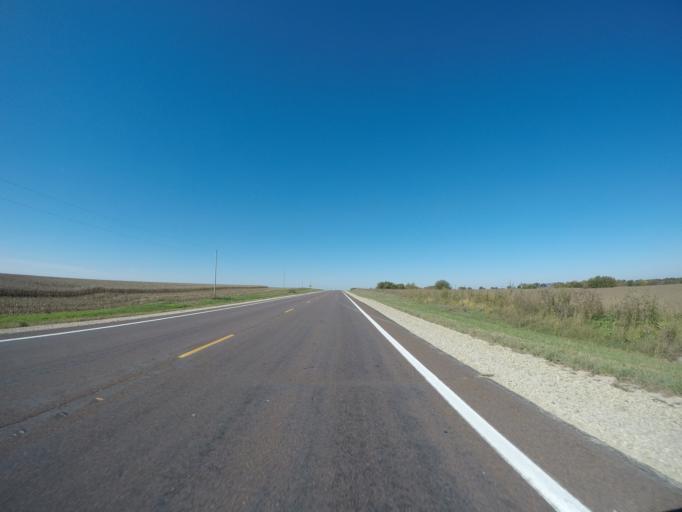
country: US
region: Kansas
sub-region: Riley County
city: Fort Riley North
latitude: 39.3064
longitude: -96.8708
